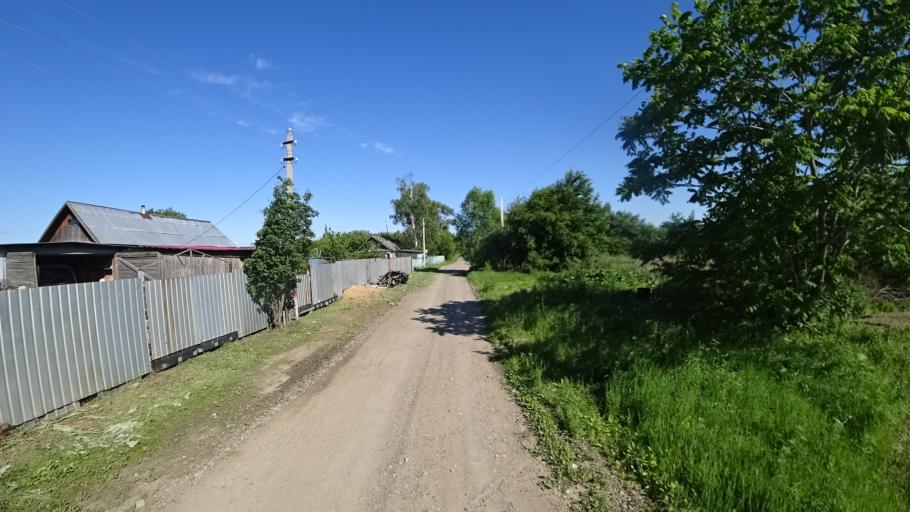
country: RU
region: Khabarovsk Krai
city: Khor
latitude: 47.8852
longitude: 135.0182
